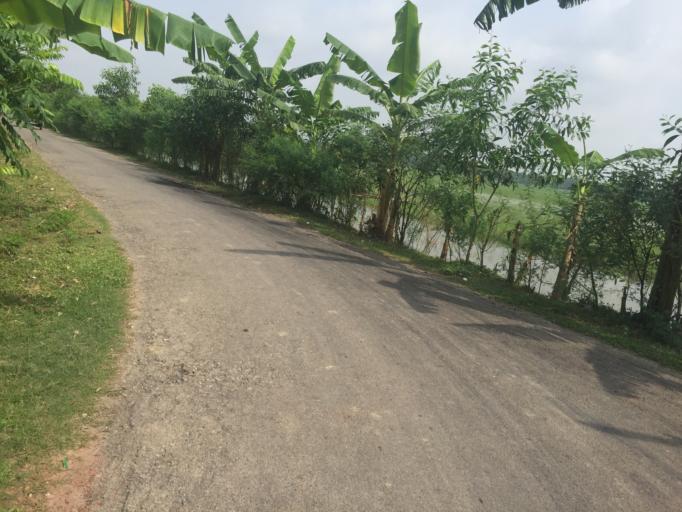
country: BD
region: Barisal
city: Mathba
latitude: 22.2523
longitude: 89.9162
